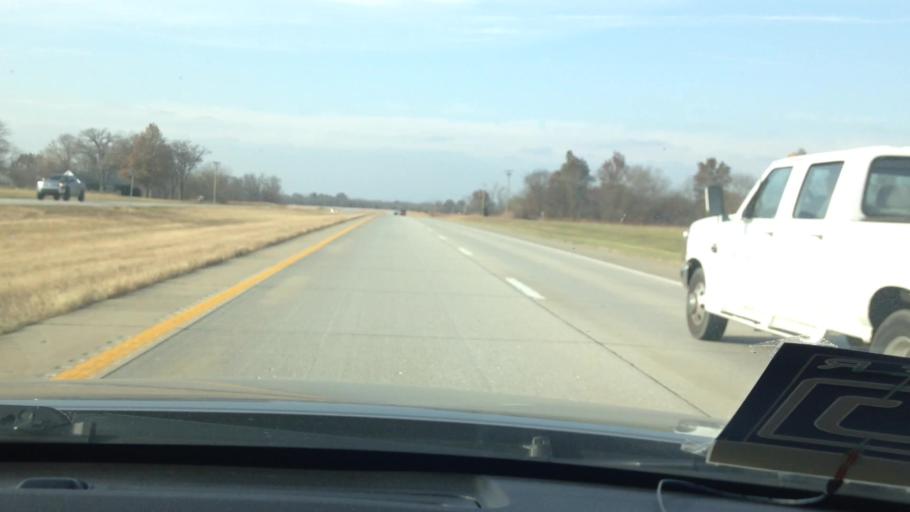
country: US
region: Missouri
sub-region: Henry County
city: Clinton
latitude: 38.4564
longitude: -93.9648
